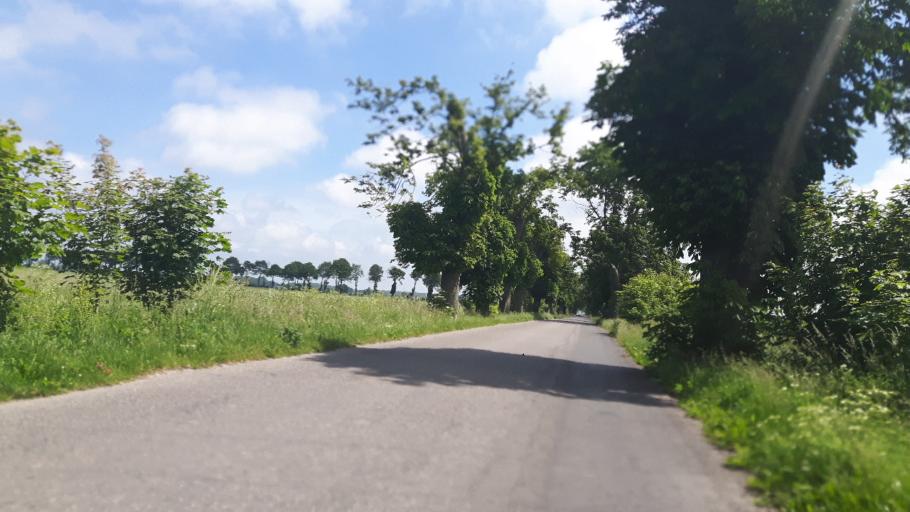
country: PL
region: West Pomeranian Voivodeship
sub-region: Powiat slawienski
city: Slawno
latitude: 54.5086
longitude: 16.5936
